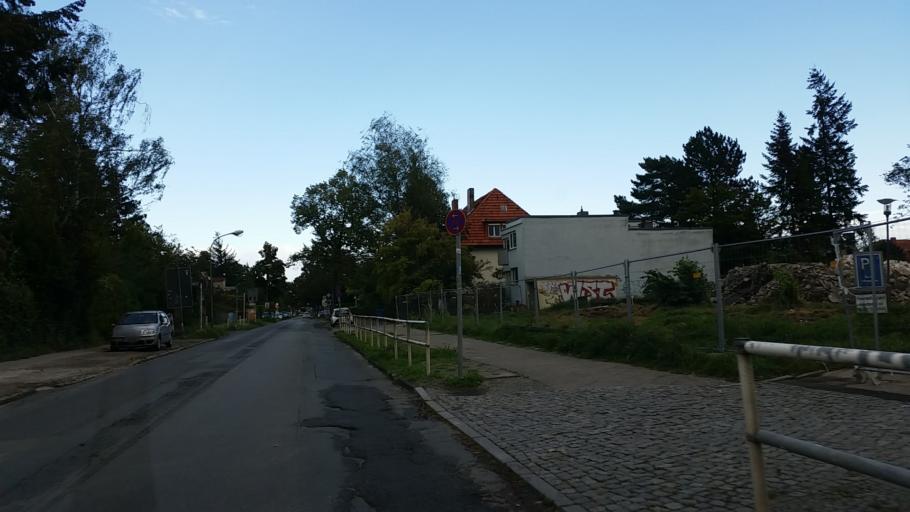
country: DE
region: Berlin
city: Lankwitz
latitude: 52.4175
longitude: 13.3334
